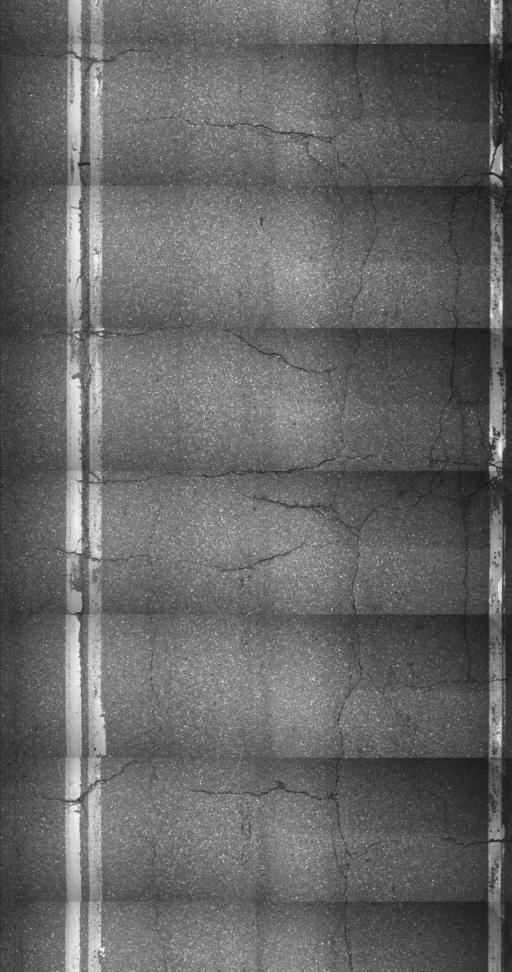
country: US
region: Vermont
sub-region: Lamoille County
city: Hyde Park
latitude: 44.7647
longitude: -72.4569
